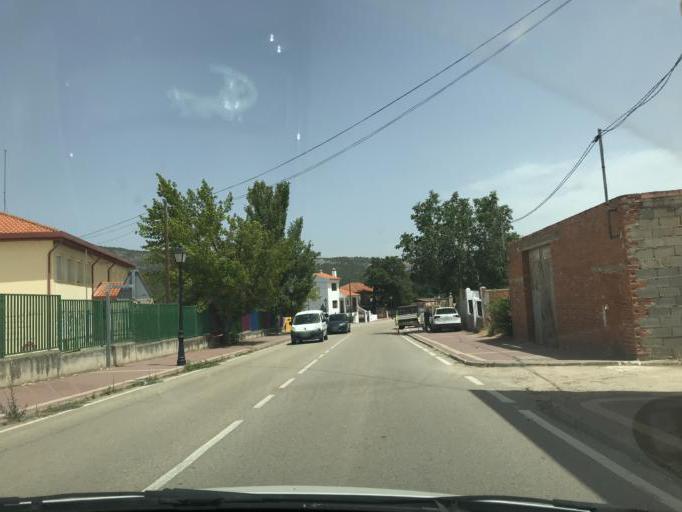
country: ES
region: Castille-La Mancha
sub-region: Provincia de Cuenca
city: Canamares
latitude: 40.4528
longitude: -2.2377
